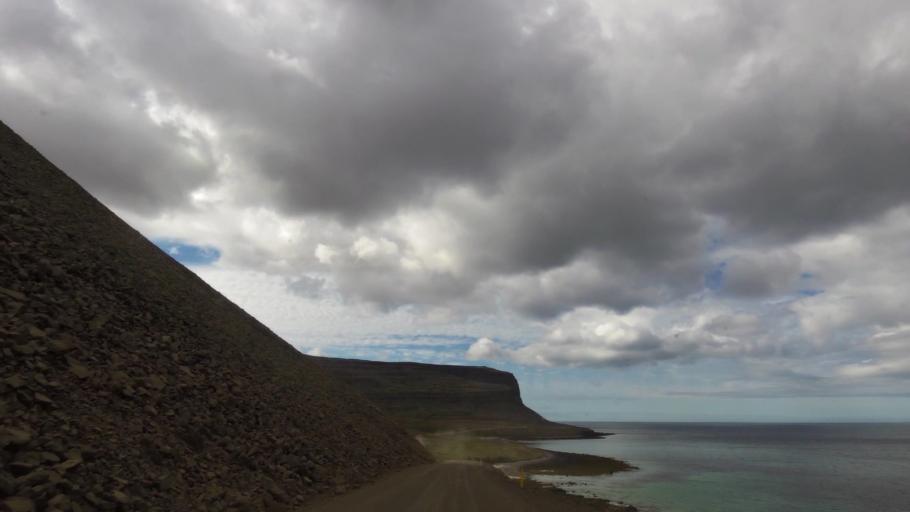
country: IS
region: West
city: Olafsvik
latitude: 65.5666
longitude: -24.0461
